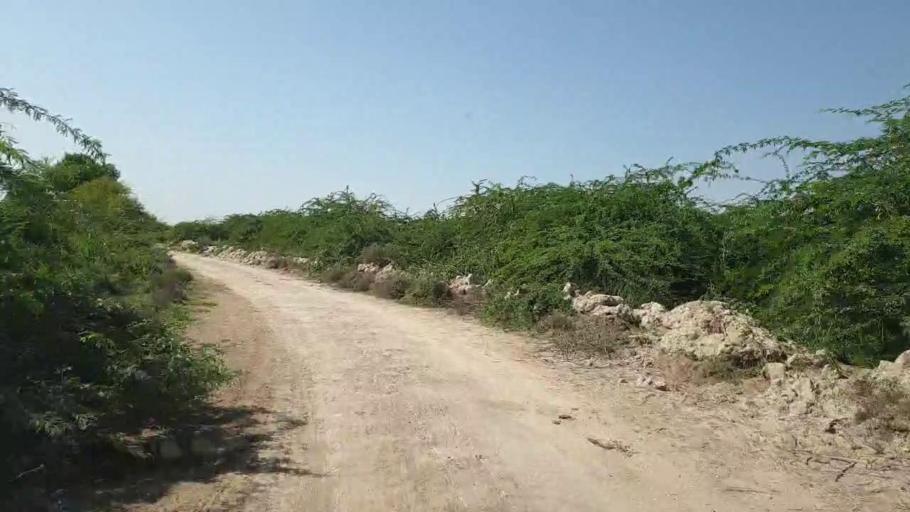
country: PK
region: Sindh
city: Tando Bago
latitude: 24.7065
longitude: 69.0502
